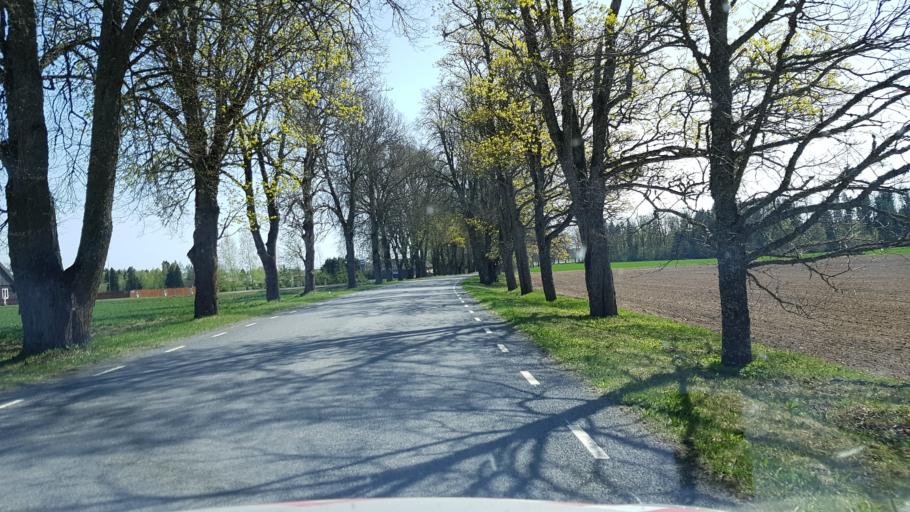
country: EE
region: Viljandimaa
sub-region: Vohma linn
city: Vohma
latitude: 58.5406
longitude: 25.5766
